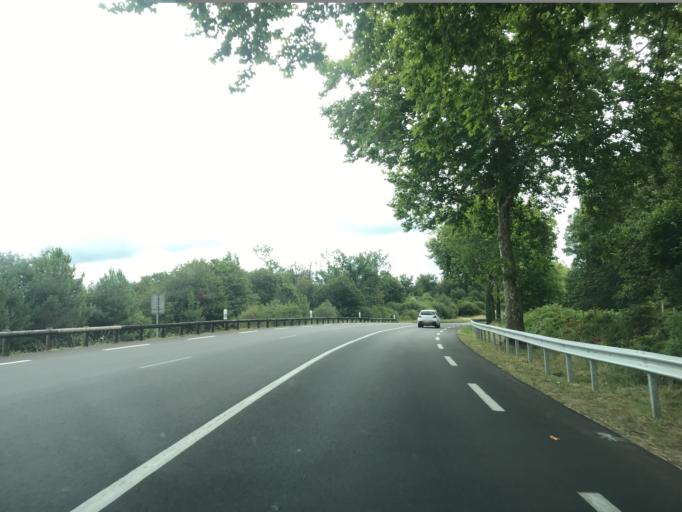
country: FR
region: Poitou-Charentes
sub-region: Departement de la Charente
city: Dignac
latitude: 45.5272
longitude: 0.2948
